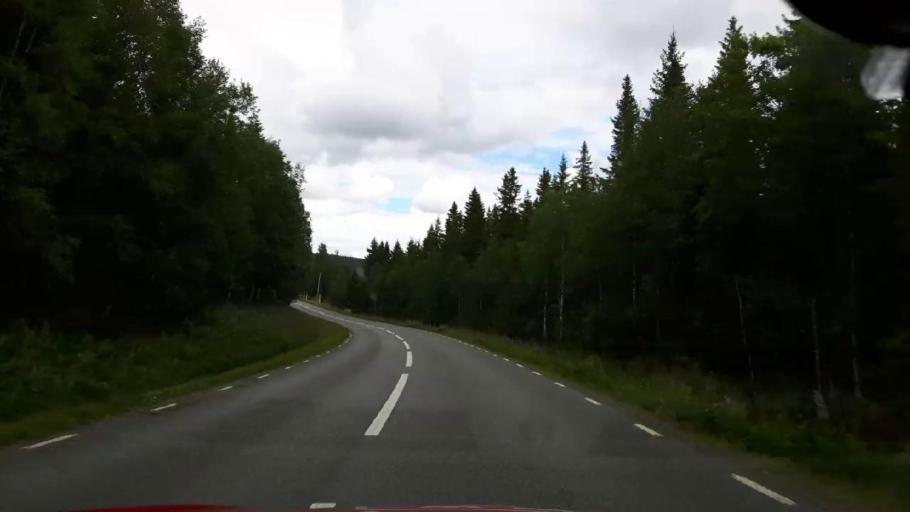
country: NO
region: Nord-Trondelag
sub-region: Lierne
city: Sandvika
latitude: 64.3911
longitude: 14.4750
